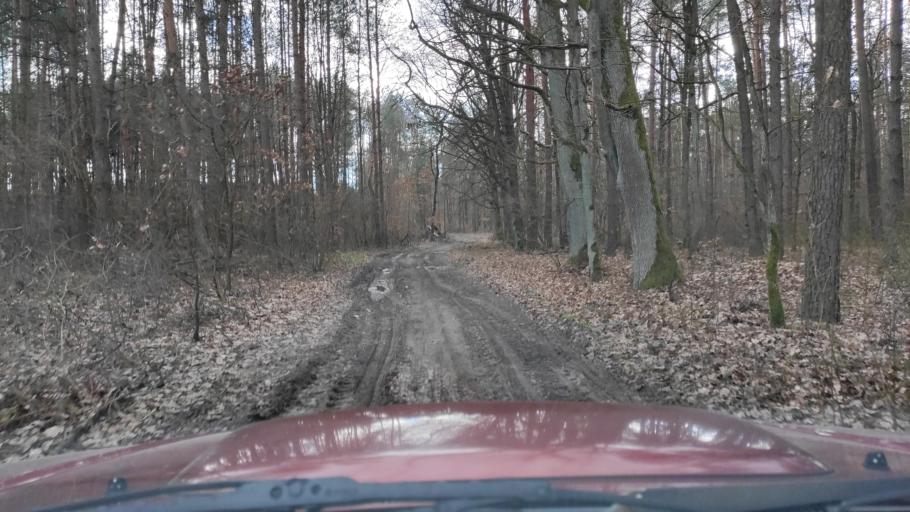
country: PL
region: Masovian Voivodeship
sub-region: Powiat kozienicki
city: Garbatka-Letnisko
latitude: 51.5144
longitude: 21.5649
